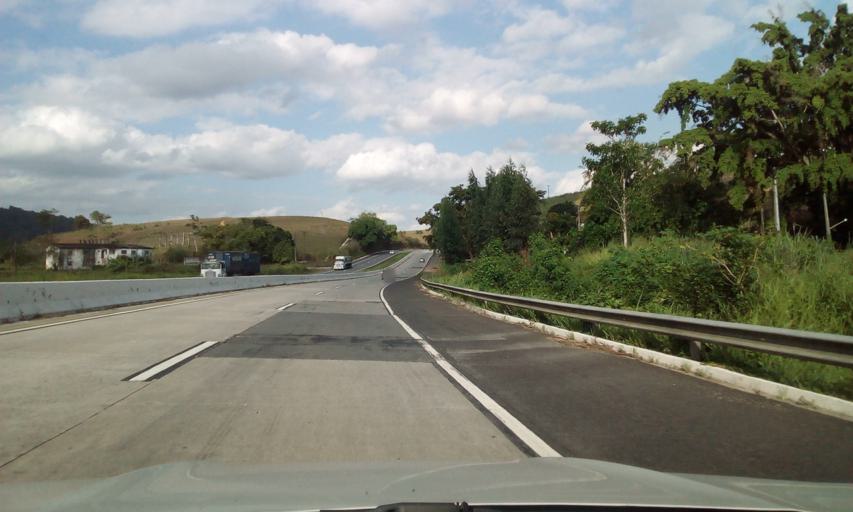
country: BR
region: Pernambuco
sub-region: Joaquim Nabuco
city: Joaquim Nabuco
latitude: -8.5788
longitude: -35.4935
